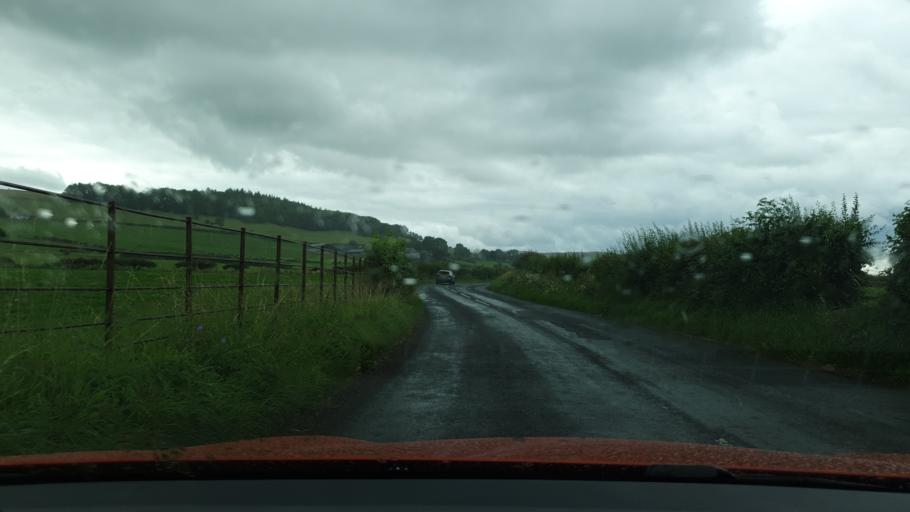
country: GB
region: England
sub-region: Cumbria
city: Penrith
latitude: 54.6270
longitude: -2.7942
